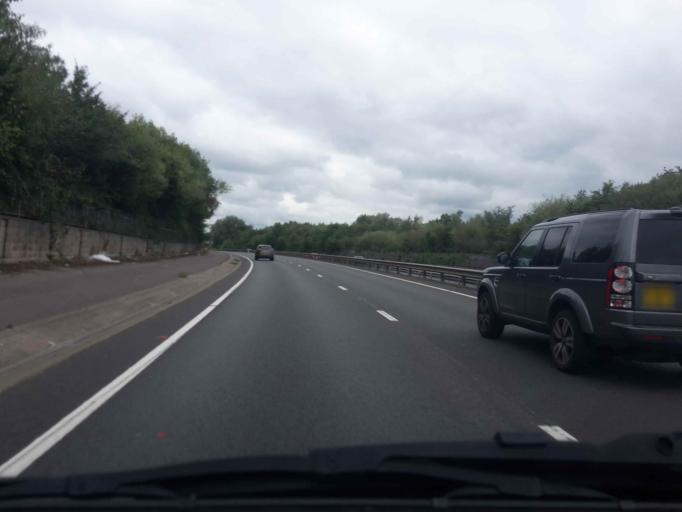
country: GB
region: England
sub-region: Surrey
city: Seale
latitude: 51.2555
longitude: -0.7303
